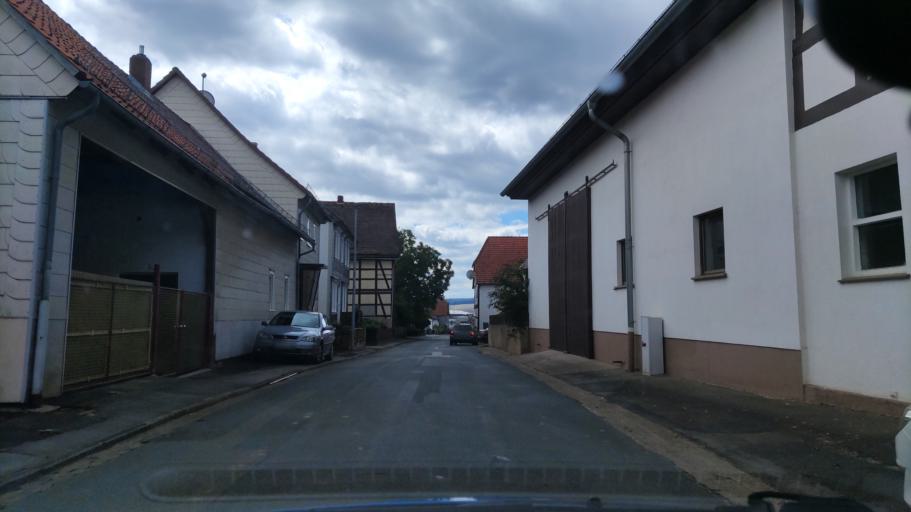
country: DE
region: Lower Saxony
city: Wangelnstedt
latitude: 51.8458
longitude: 9.7244
